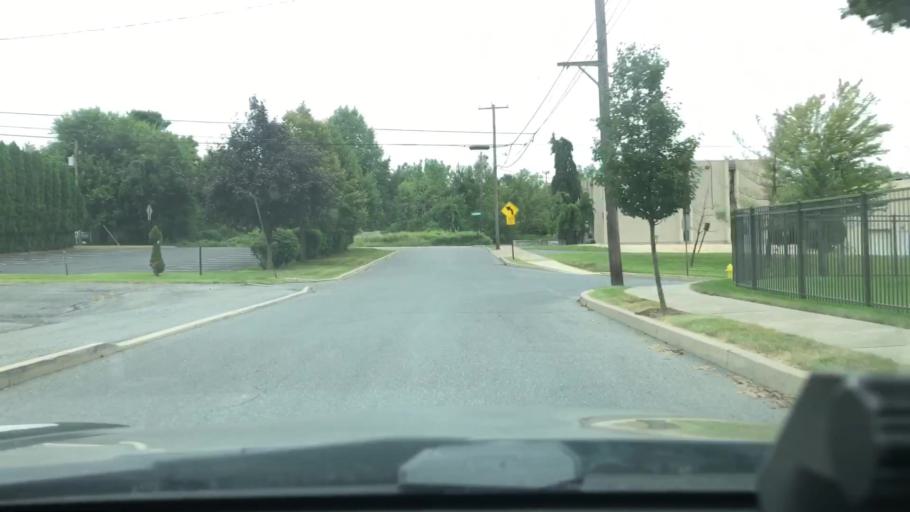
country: US
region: Pennsylvania
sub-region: Lehigh County
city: Fullerton
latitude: 40.6188
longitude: -75.4480
